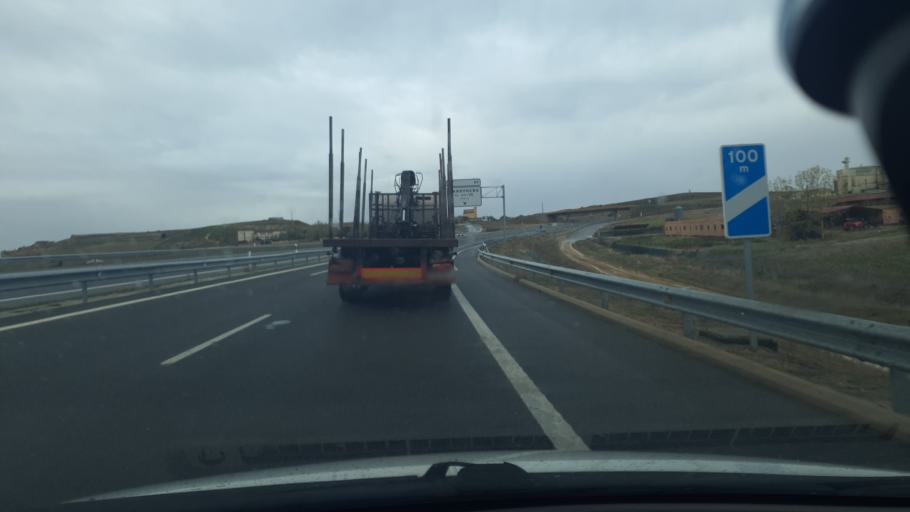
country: ES
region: Castille and Leon
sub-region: Provincia de Segovia
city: Tabanera la Luenga
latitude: 41.1086
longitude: -4.2506
